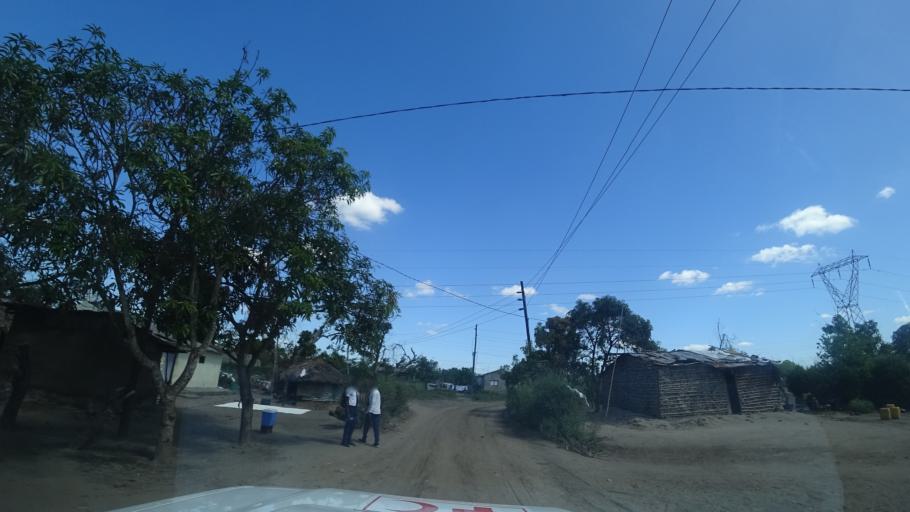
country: MZ
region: Sofala
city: Dondo
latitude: -19.4962
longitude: 34.5971
